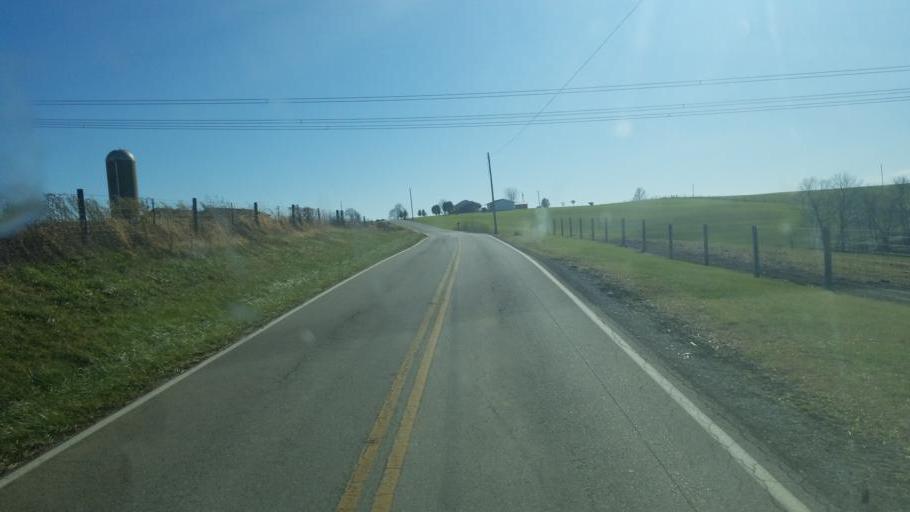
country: US
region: Kentucky
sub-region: Mason County
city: Maysville
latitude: 38.5480
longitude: -83.6399
